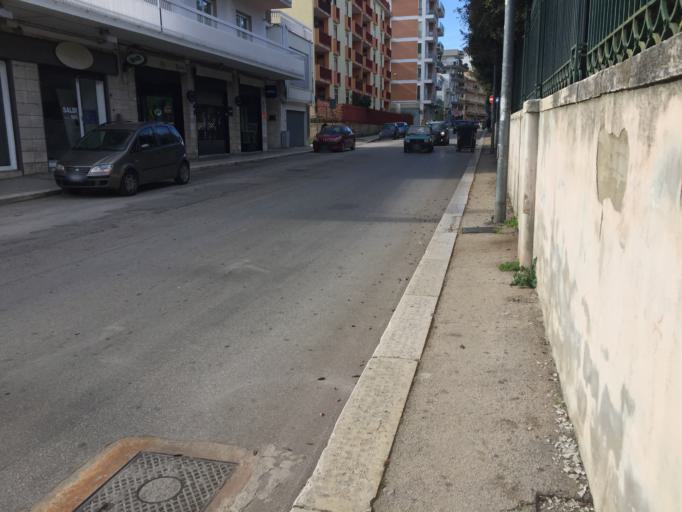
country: IT
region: Apulia
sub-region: Provincia di Bari
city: Bitonto
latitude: 41.1121
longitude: 16.6977
